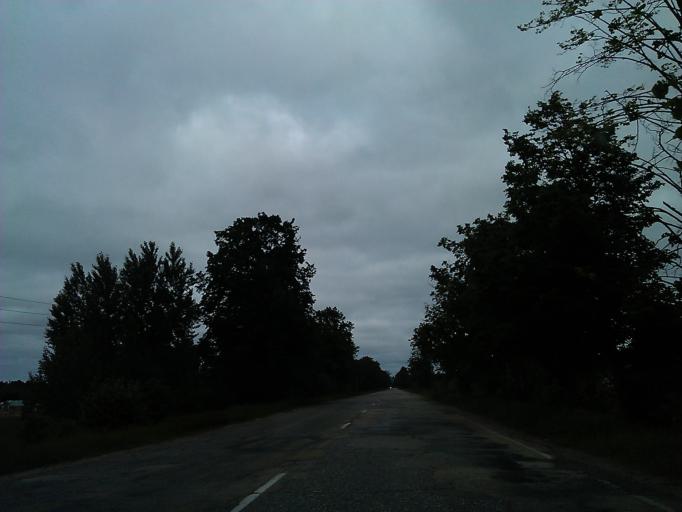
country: LV
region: Adazi
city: Adazi
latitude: 57.1027
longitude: 24.3105
